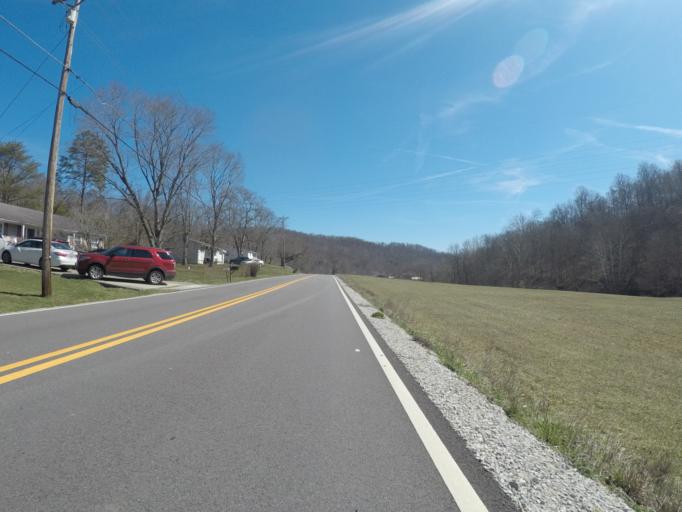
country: US
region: Ohio
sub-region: Lawrence County
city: Burlington
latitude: 38.4483
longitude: -82.5094
